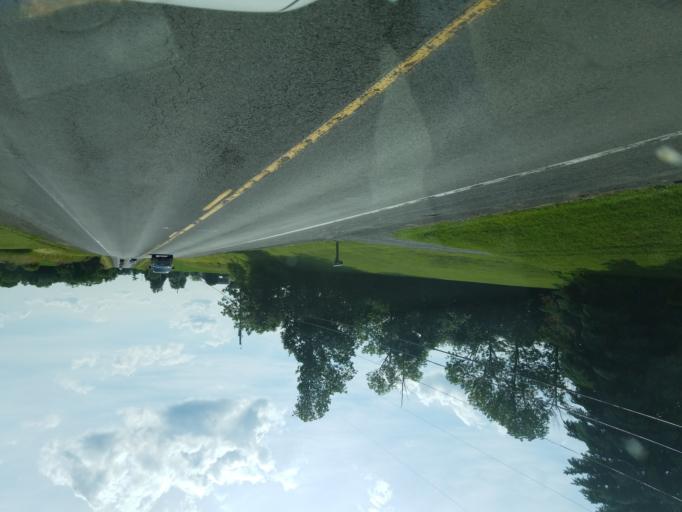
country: US
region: New York
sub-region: Ontario County
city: Shortsville
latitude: 42.8615
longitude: -77.1775
